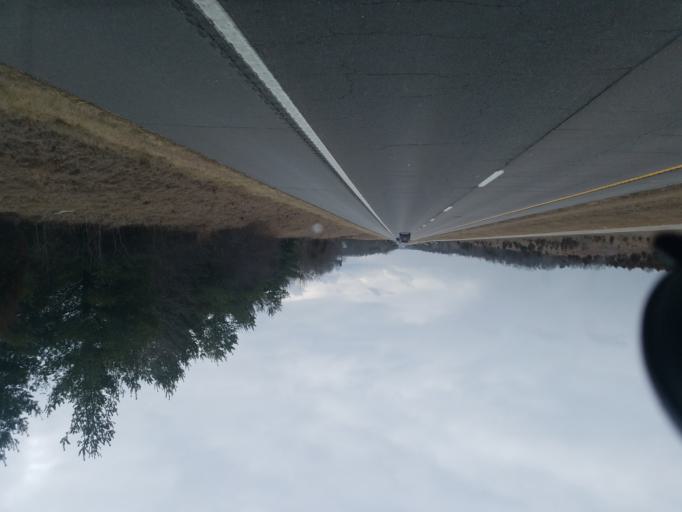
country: US
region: Missouri
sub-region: Boone County
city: Hallsville
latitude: 39.0883
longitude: -92.3298
